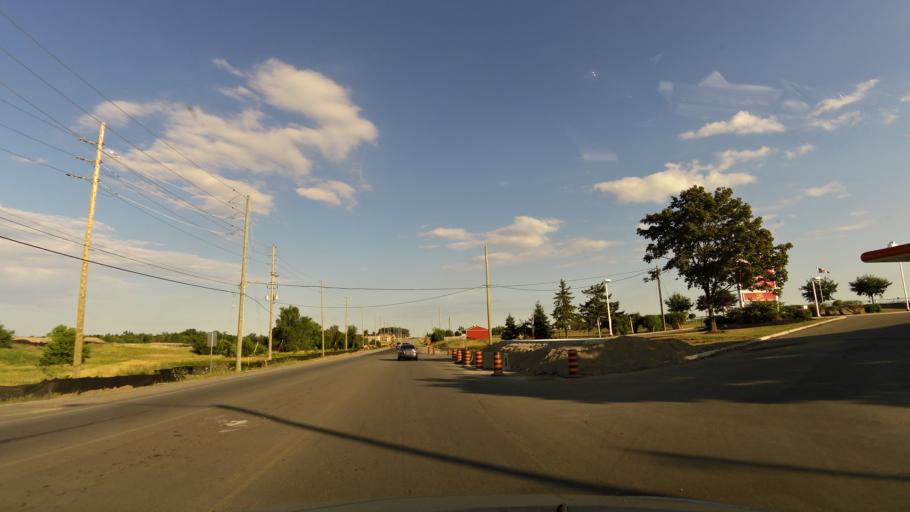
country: CA
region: Ontario
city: Brampton
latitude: 43.6668
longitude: -79.8293
